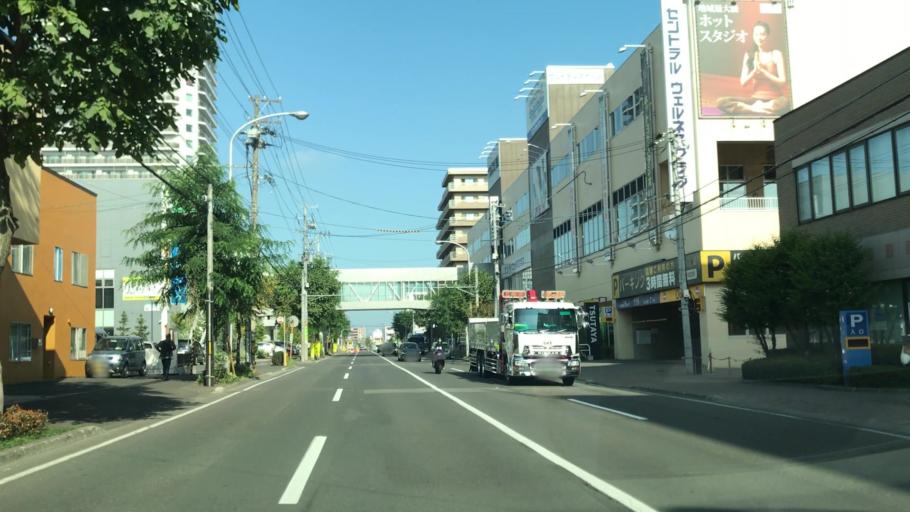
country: JP
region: Hokkaido
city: Sapporo
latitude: 43.0812
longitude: 141.3042
